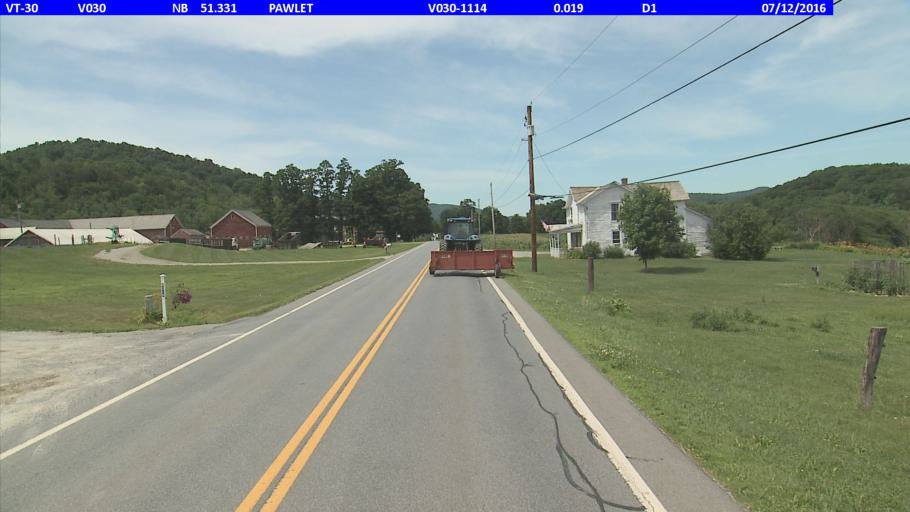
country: US
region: New York
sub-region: Washington County
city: Granville
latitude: 43.3117
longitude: -73.1687
